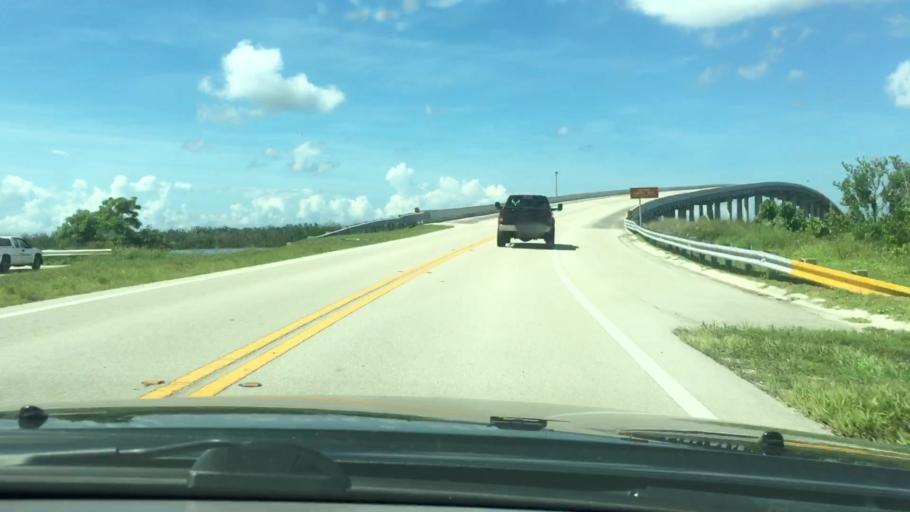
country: US
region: Florida
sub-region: Collier County
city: Marco
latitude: 25.9337
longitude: -81.6500
